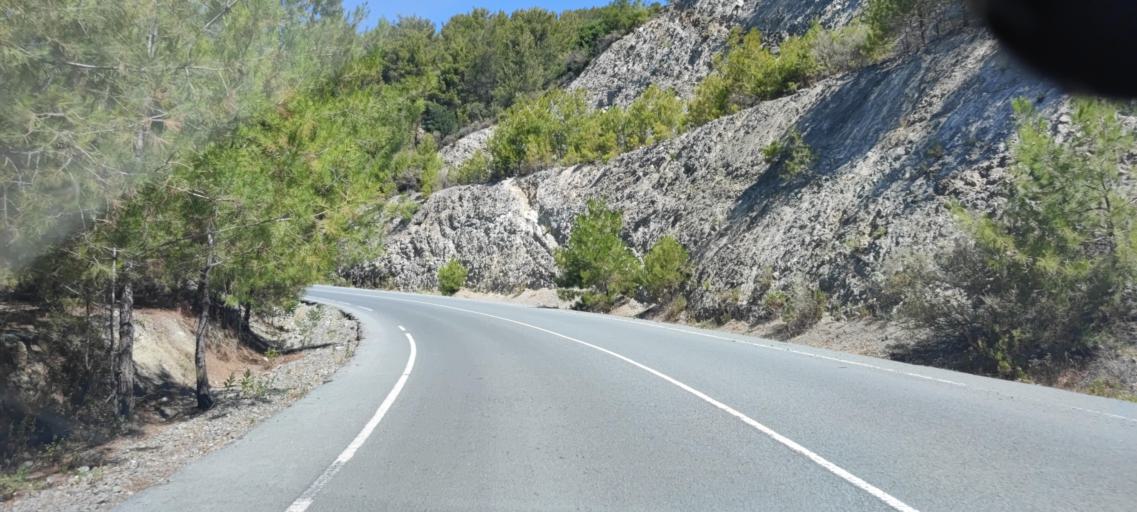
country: CY
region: Limassol
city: Pachna
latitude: 34.8990
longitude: 32.8187
